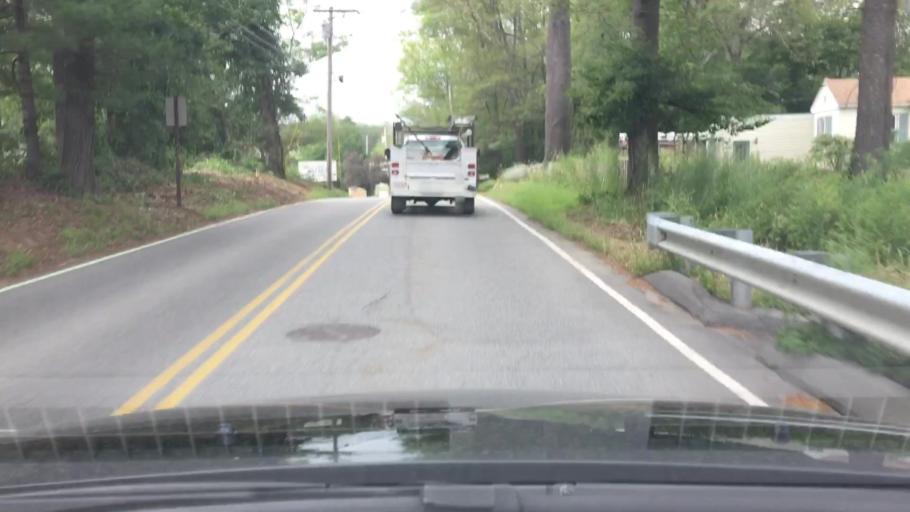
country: US
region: Massachusetts
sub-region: Worcester County
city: Northborough
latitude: 42.2907
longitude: -71.6566
